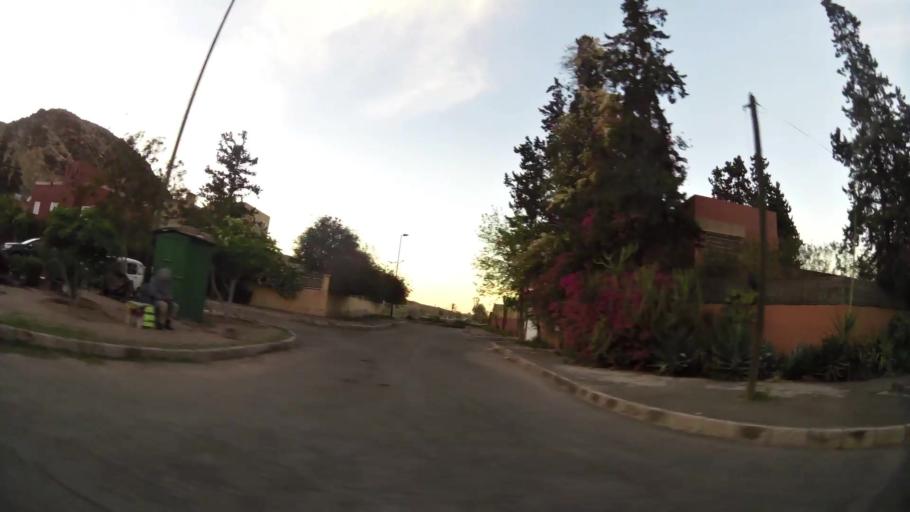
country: MA
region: Marrakech-Tensift-Al Haouz
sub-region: Marrakech
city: Marrakesh
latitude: 31.6446
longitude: -8.0234
